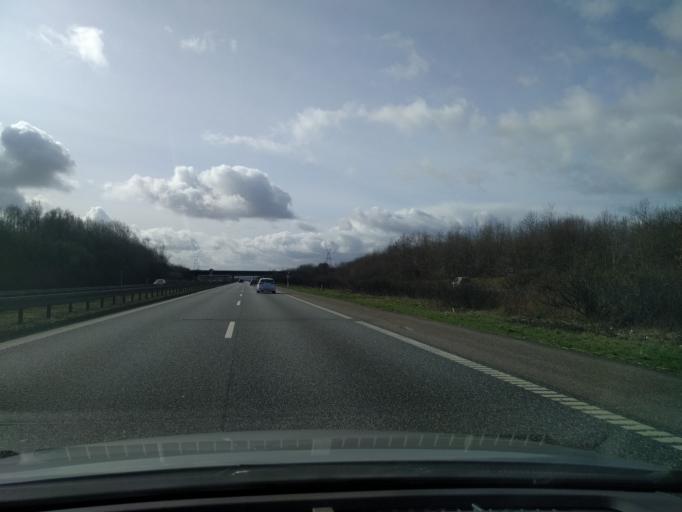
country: DK
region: South Denmark
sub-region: Kolding Kommune
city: Kolding
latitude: 55.5169
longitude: 9.4440
